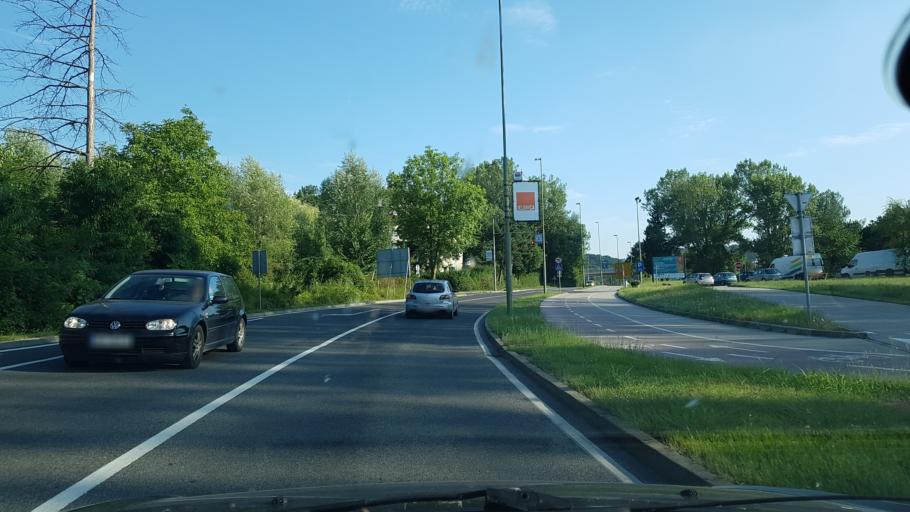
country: SI
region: Nova Gorica
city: Nova Gorica
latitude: 45.9576
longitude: 13.6529
